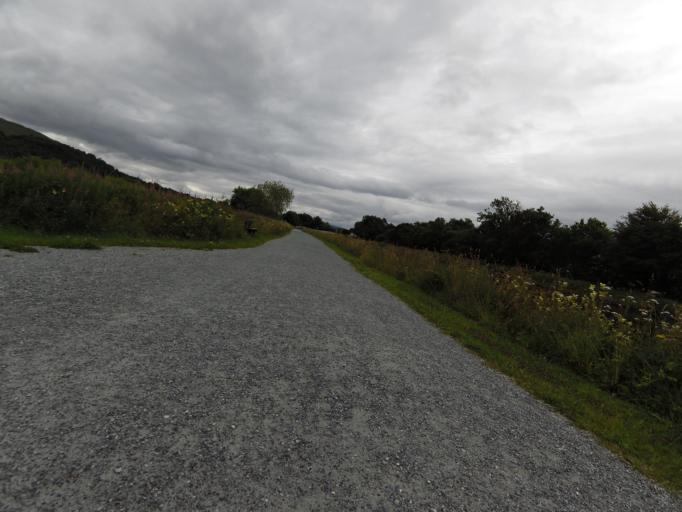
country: GB
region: Scotland
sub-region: Highland
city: Fort William
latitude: 56.8427
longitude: -5.1019
